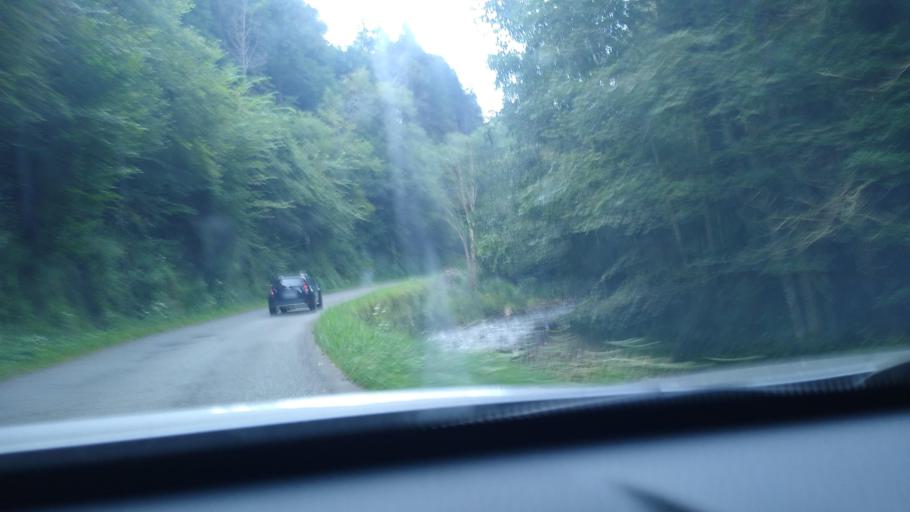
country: FR
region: Midi-Pyrenees
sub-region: Departement de l'Ariege
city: Saint-Girons
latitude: 42.8070
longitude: 1.1963
